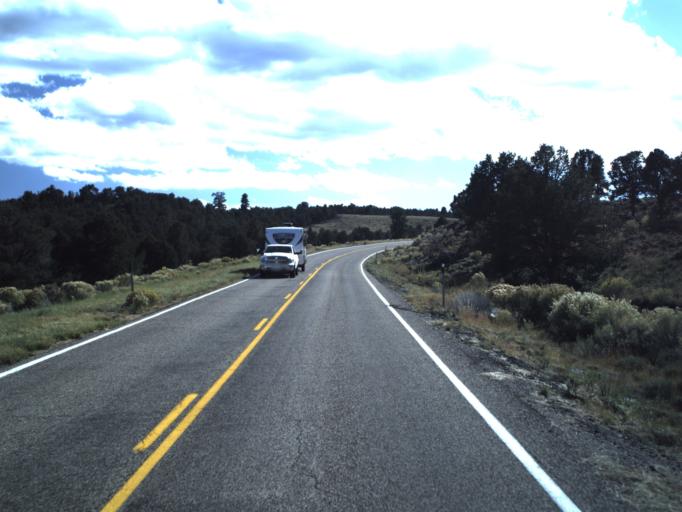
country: US
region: Utah
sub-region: Garfield County
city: Panguitch
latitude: 37.7847
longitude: -112.4396
